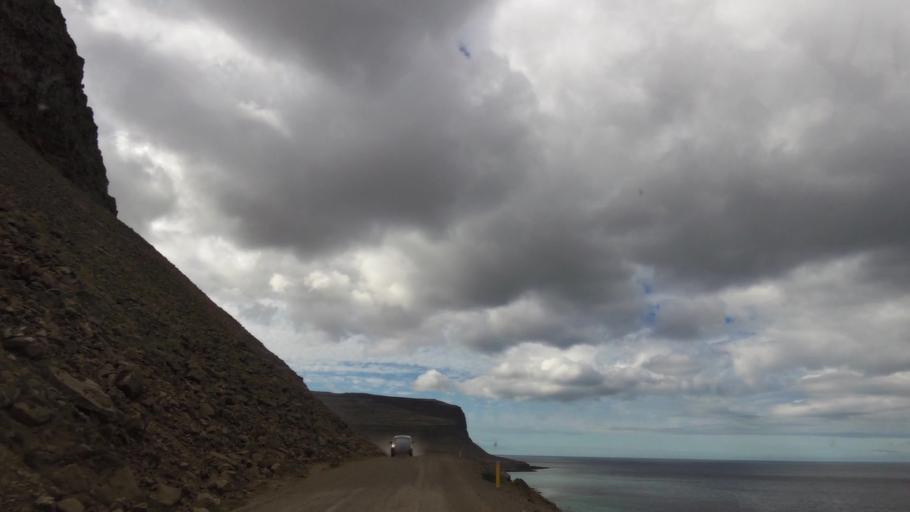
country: IS
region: West
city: Olafsvik
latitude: 65.5662
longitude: -24.0431
